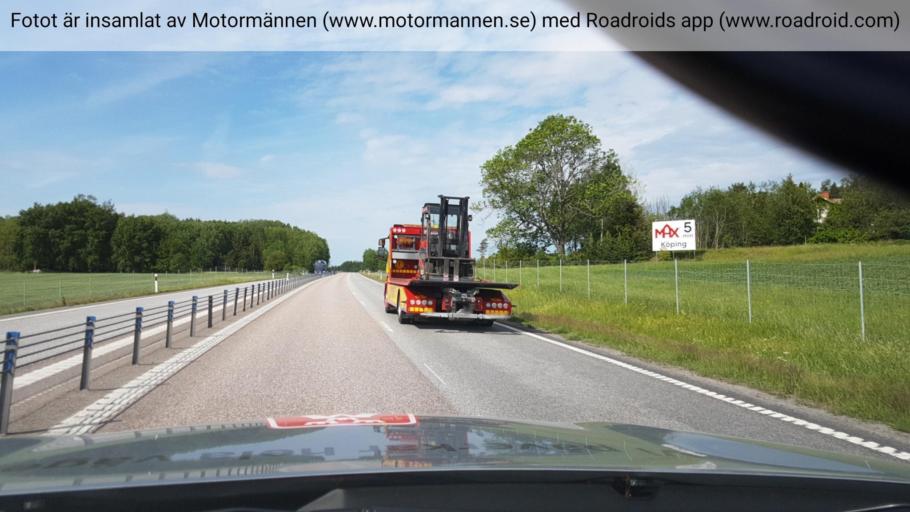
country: SE
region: Vaestmanland
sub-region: Kopings Kommun
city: Koping
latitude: 59.5545
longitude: 16.0403
